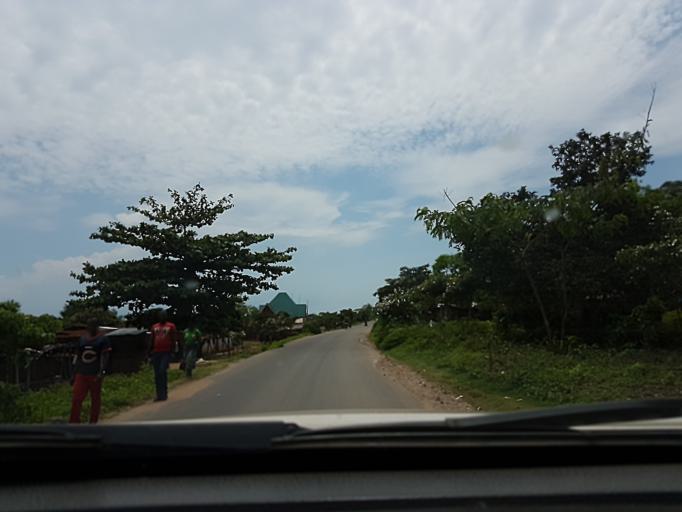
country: CD
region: South Kivu
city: Uvira
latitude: -3.2442
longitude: 29.1611
